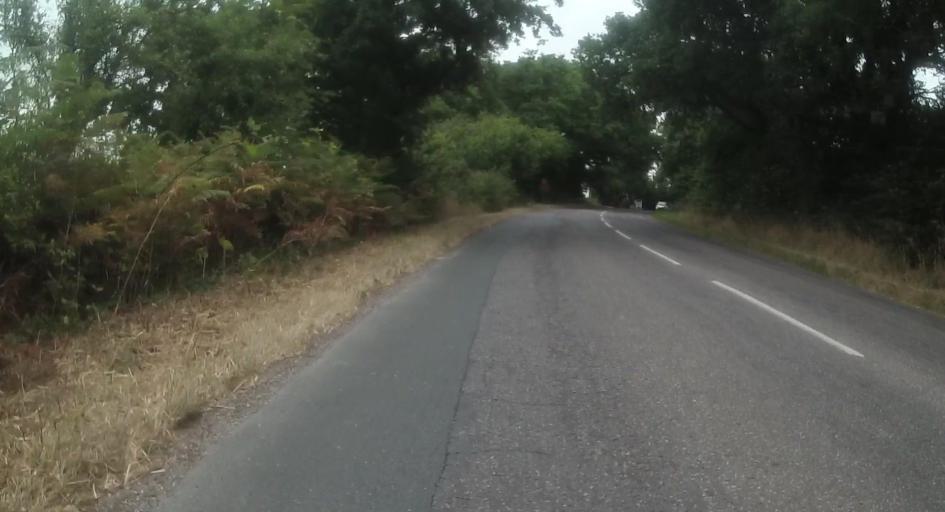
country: GB
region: England
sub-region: Dorset
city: Bovington Camp
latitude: 50.7415
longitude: -2.2203
